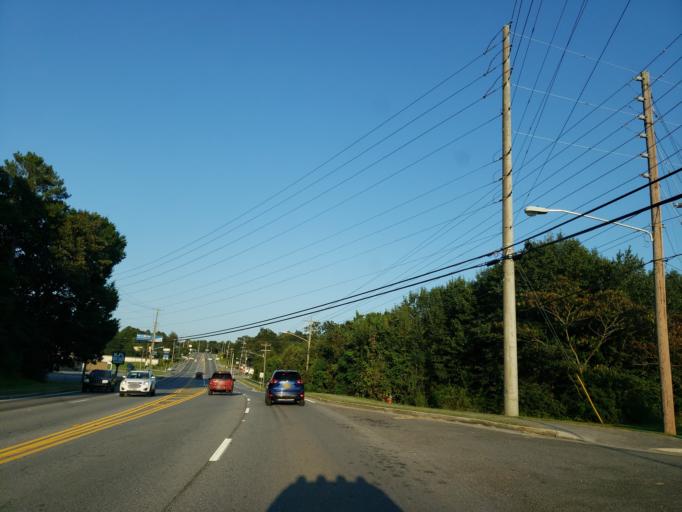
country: US
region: Georgia
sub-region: Gordon County
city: Calhoun
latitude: 34.5123
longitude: -84.9376
